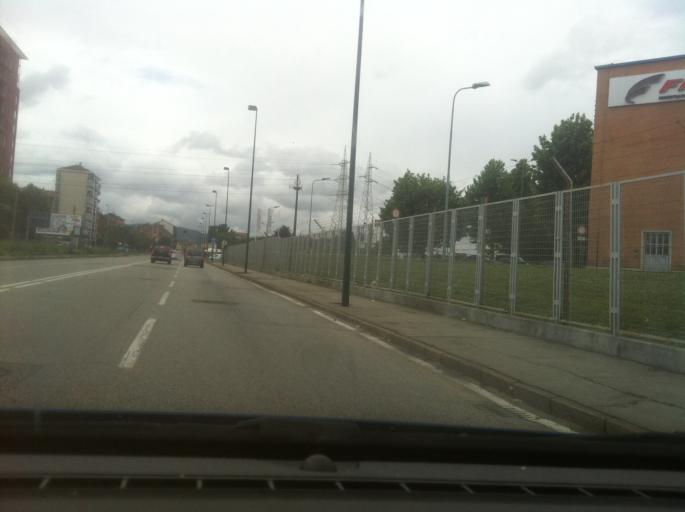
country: IT
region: Piedmont
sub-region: Provincia di Torino
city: San Mauro Torinese
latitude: 45.1093
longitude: 7.7286
